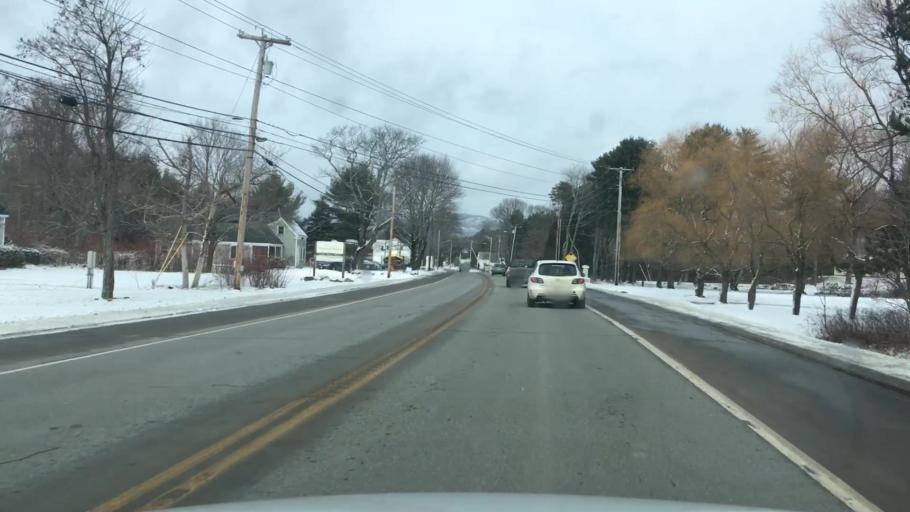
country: US
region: Maine
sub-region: Knox County
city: Rockport
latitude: 44.1711
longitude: -69.0801
